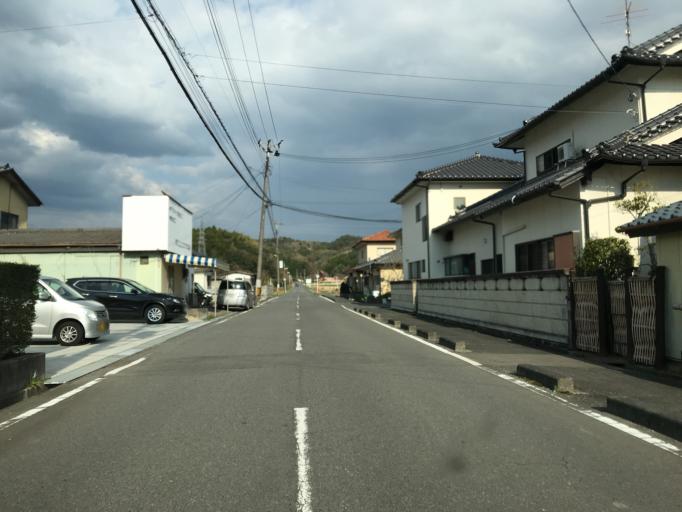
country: JP
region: Fukushima
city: Iwaki
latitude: 37.0880
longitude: 140.8786
